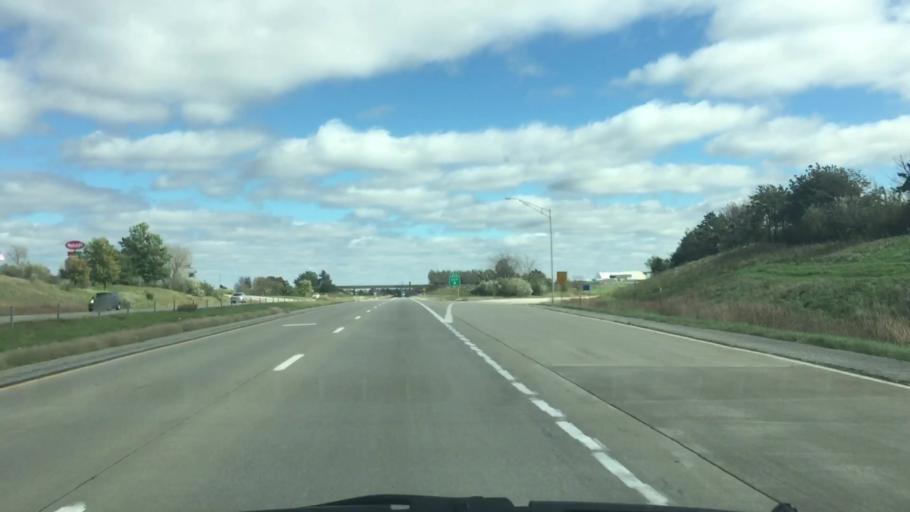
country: US
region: Iowa
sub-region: Iowa County
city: Williamsburg
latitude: 41.6893
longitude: -92.0734
